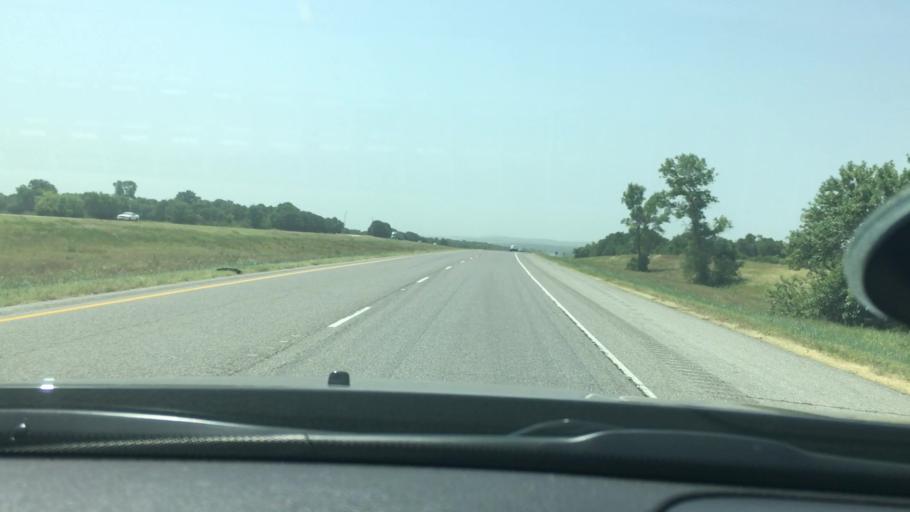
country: US
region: Oklahoma
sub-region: Murray County
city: Davis
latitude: 34.5569
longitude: -97.1928
